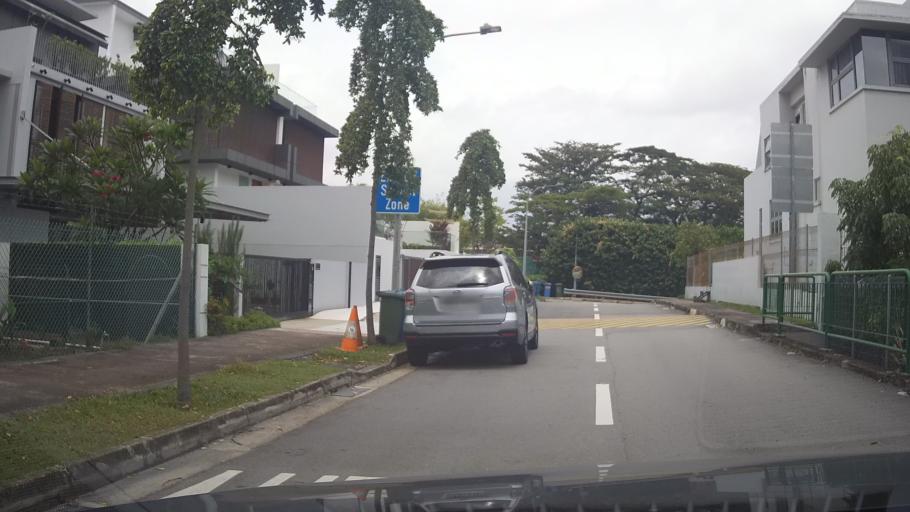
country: SG
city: Singapore
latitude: 1.3065
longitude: 103.8907
